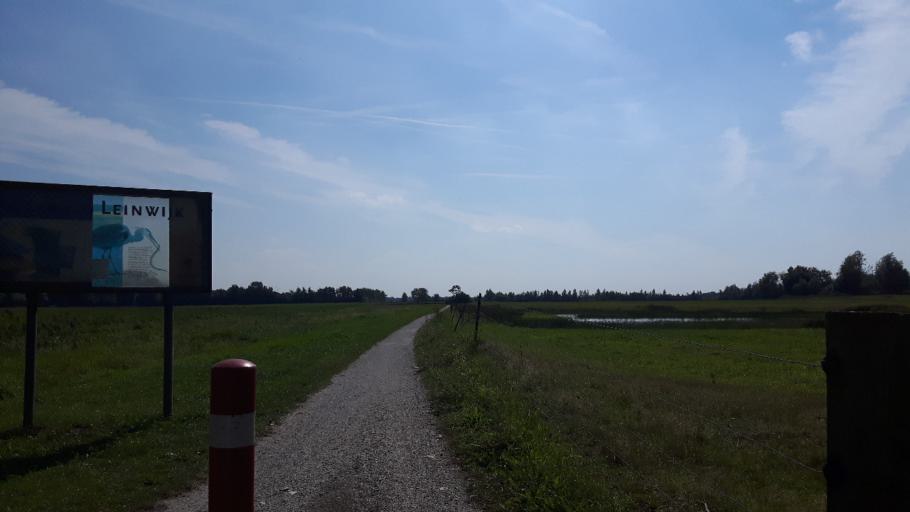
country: NL
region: Groningen
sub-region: Gemeente Hoogezand-Sappemeer
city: Hoogezand
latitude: 53.1373
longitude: 6.7194
